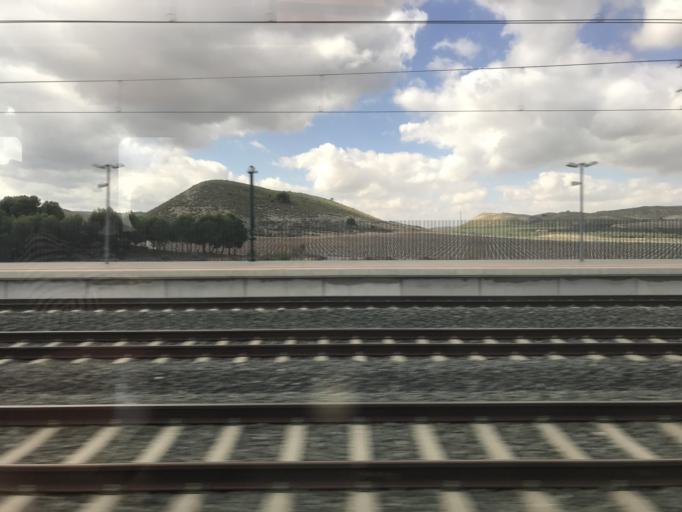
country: ES
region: Valencia
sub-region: Provincia de Alicante
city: Villena
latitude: 38.5871
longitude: -0.8747
